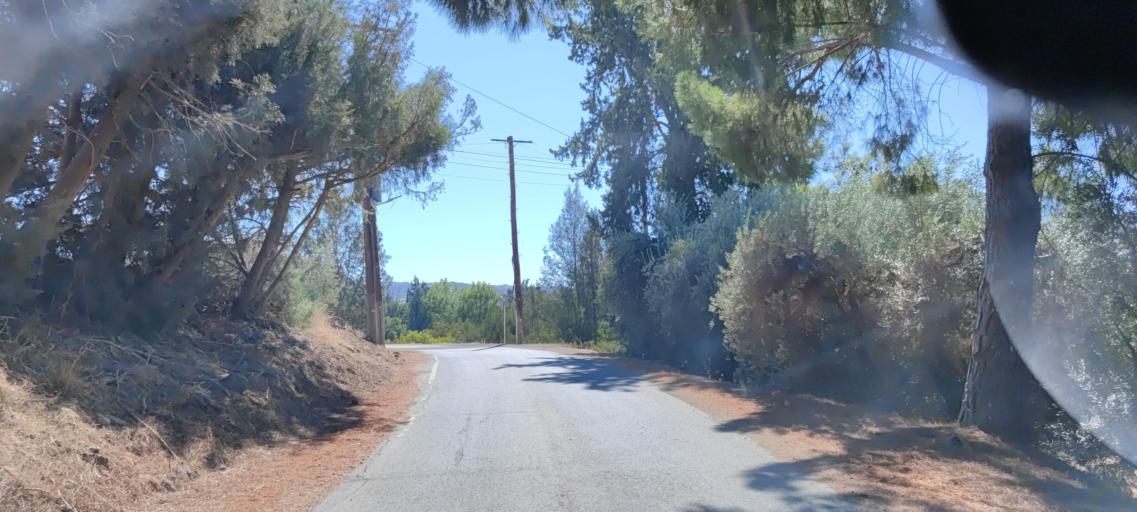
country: CY
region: Limassol
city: Mouttagiaka
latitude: 34.7595
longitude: 33.1060
